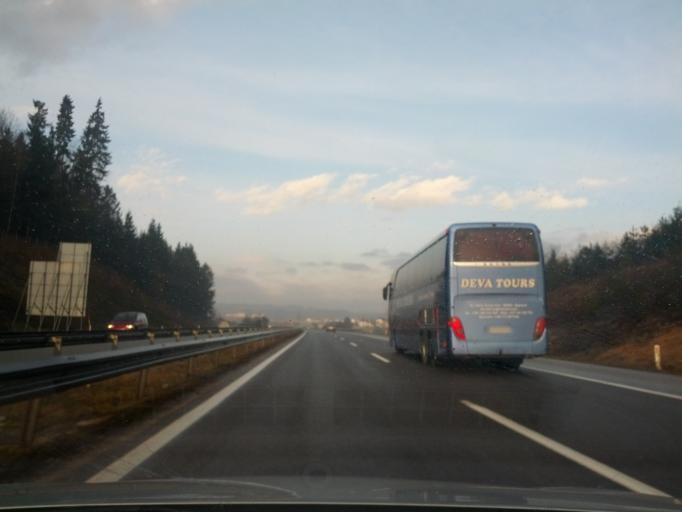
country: SI
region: Naklo
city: Naklo
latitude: 46.2716
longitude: 14.3276
